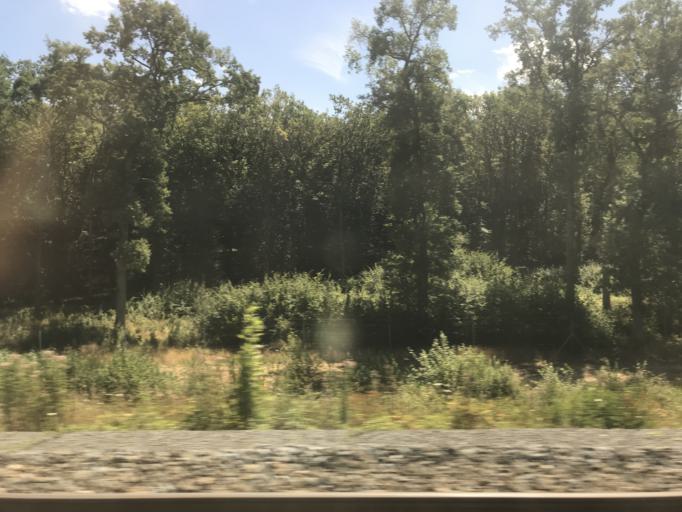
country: FR
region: Lorraine
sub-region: Departement de la Moselle
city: Solgne
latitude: 48.9611
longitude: 6.3239
